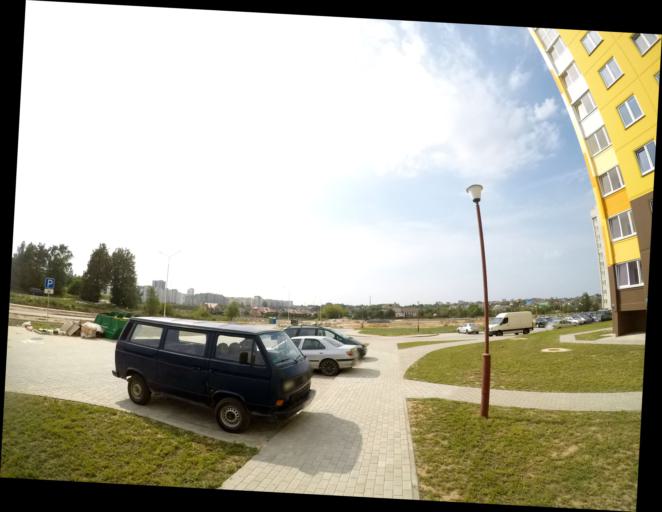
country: BY
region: Grodnenskaya
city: Hrodna
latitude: 53.7177
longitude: 23.8639
